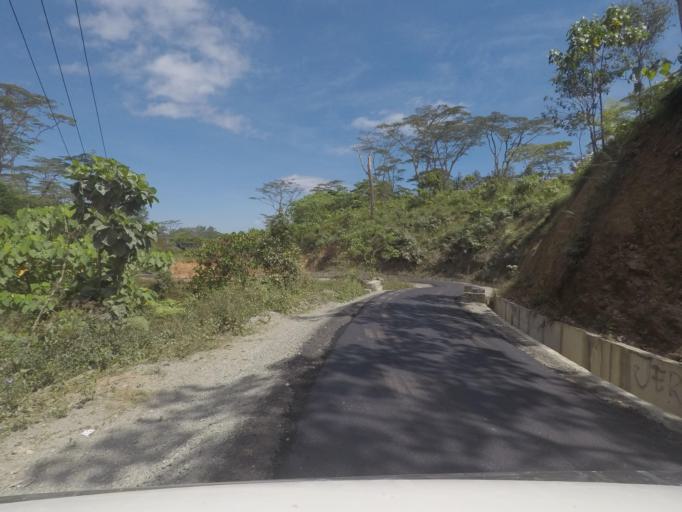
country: TL
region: Ermera
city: Gleno
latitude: -8.7501
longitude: 125.3407
